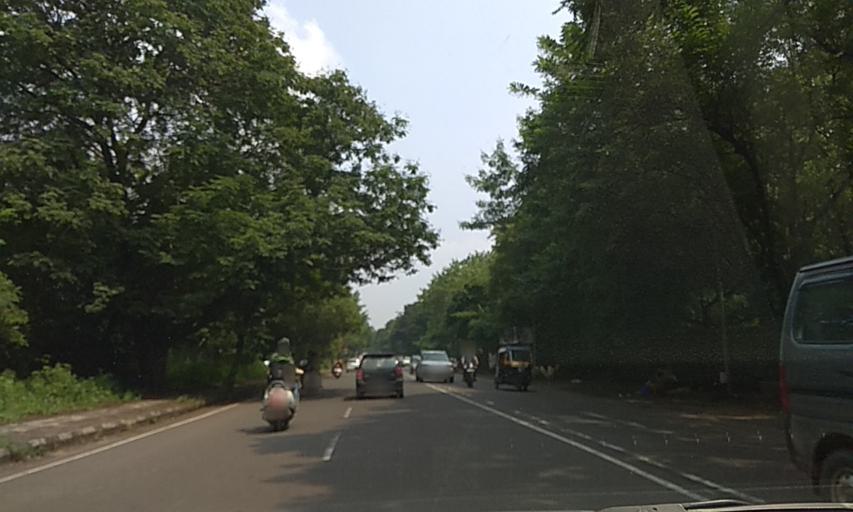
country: IN
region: Maharashtra
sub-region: Pune Division
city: Shivaji Nagar
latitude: 18.5397
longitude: 73.8136
